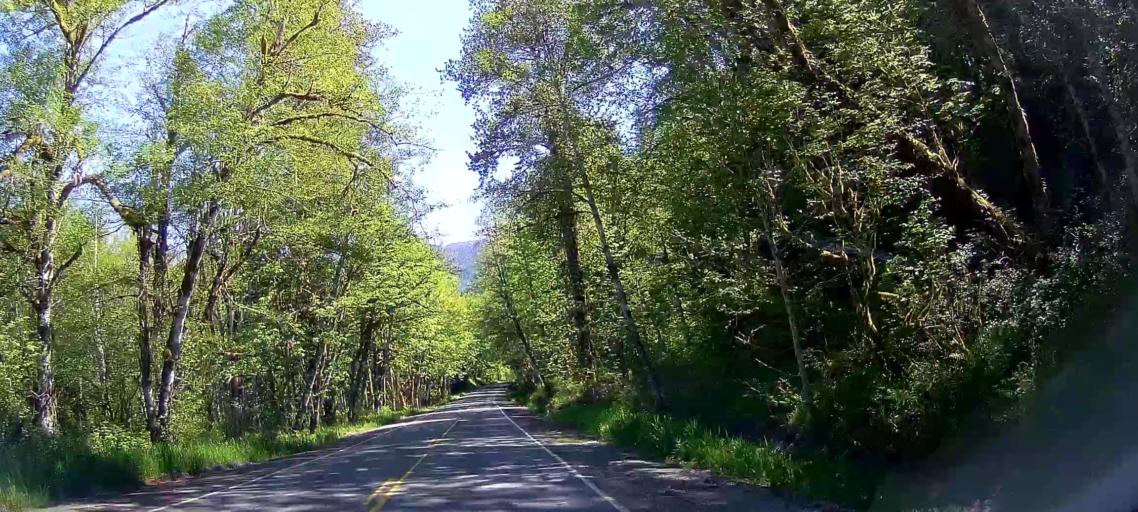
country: US
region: Washington
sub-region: Snohomish County
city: Darrington
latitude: 48.5070
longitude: -121.6906
